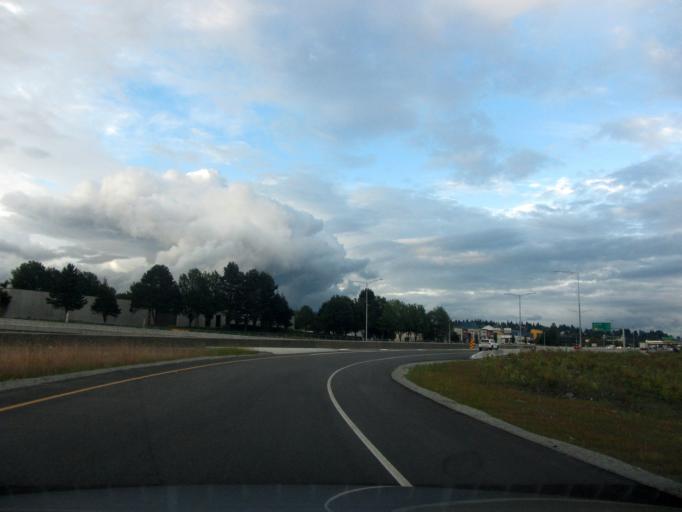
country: CA
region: British Columbia
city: New Westminster
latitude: 49.2336
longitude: -122.8764
